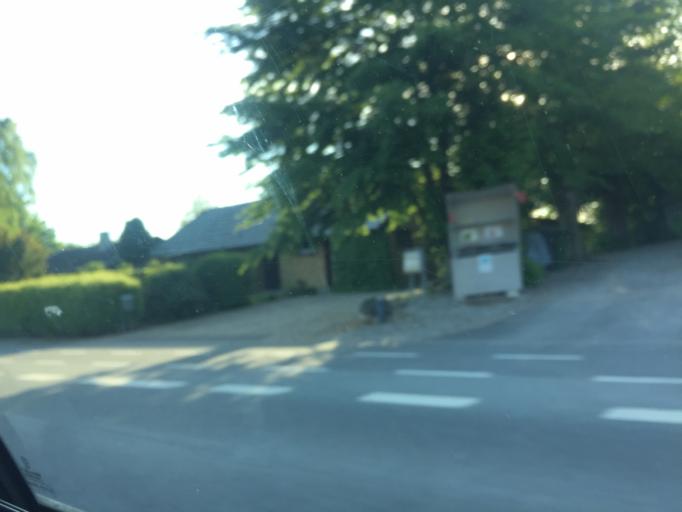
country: DK
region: South Denmark
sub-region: Nyborg Kommune
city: Ullerslev
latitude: 55.2833
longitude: 10.6910
